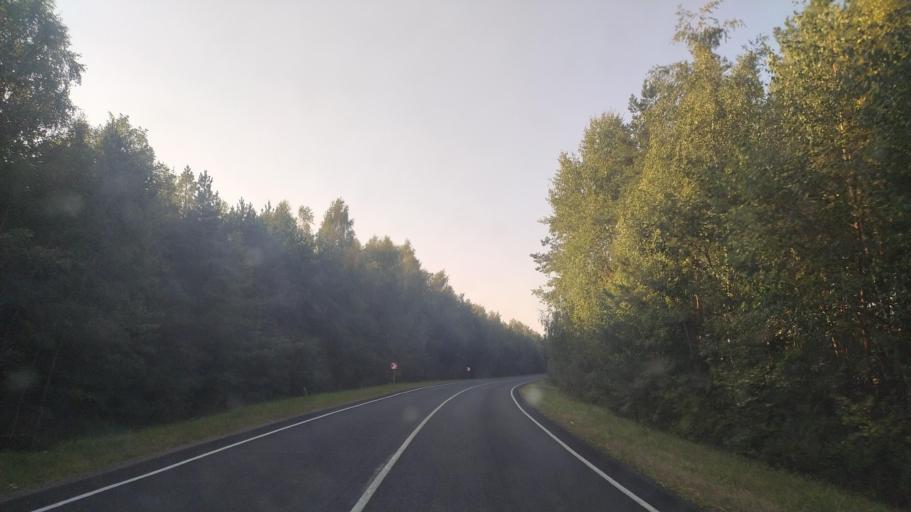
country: BY
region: Brest
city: Drahichyn
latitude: 52.2778
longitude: 25.0718
